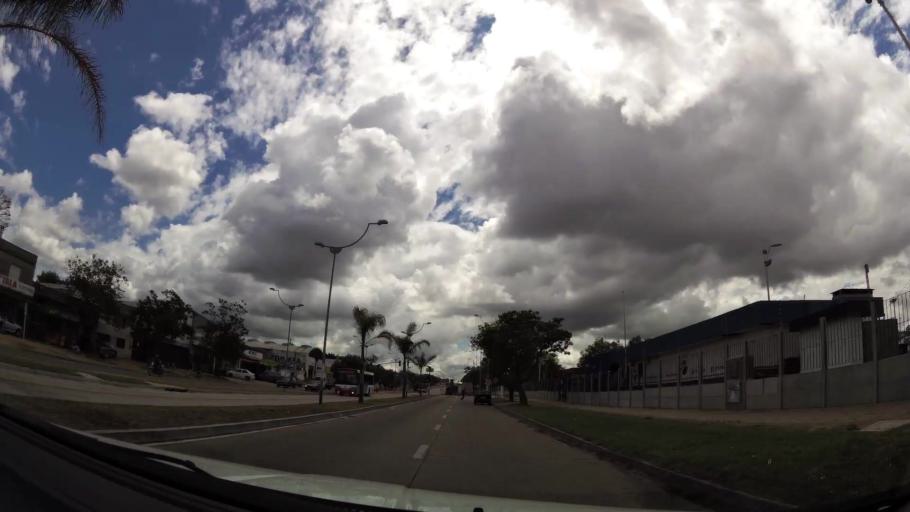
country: UY
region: Montevideo
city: Montevideo
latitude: -34.8436
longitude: -56.1531
